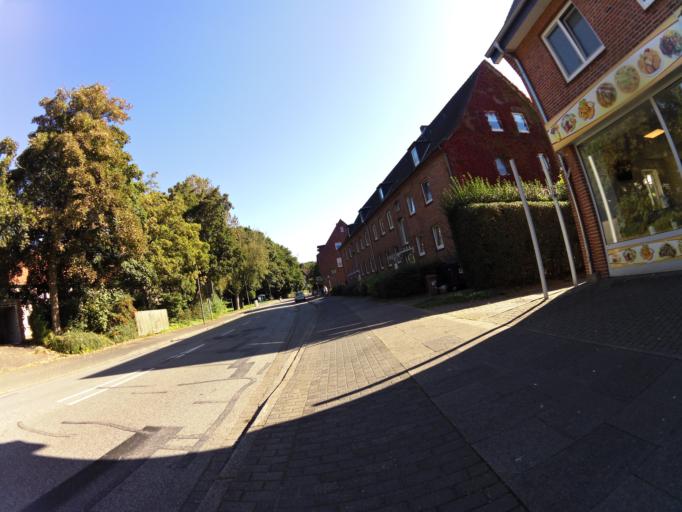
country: DE
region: Schleswig-Holstein
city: Eckernforde
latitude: 54.4552
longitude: 9.8365
